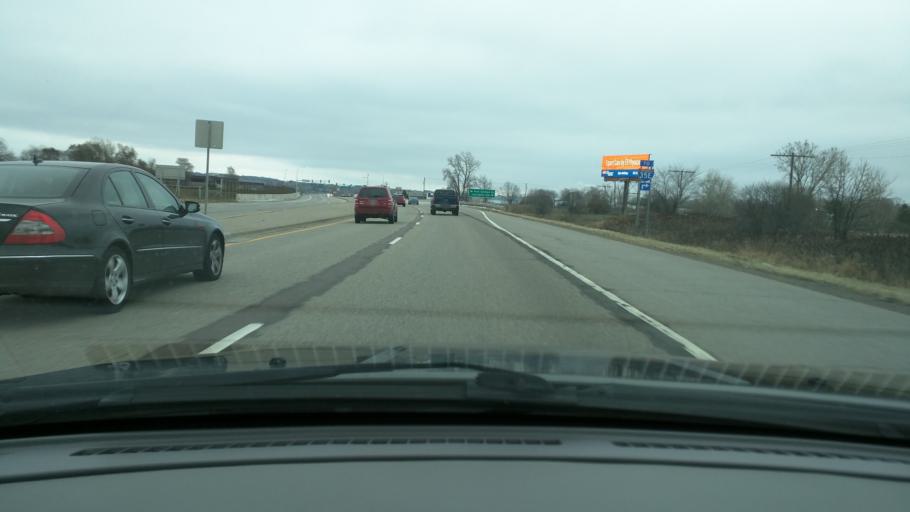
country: US
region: Minnesota
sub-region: Dakota County
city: Mendota Heights
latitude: 44.8600
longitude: -93.1483
